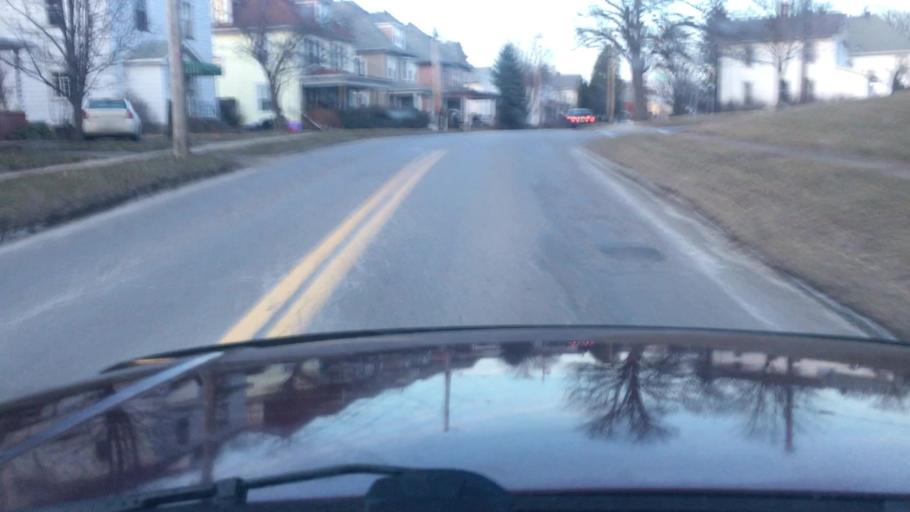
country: US
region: Pennsylvania
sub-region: Mercer County
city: Grove City
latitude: 41.1569
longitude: -80.0927
